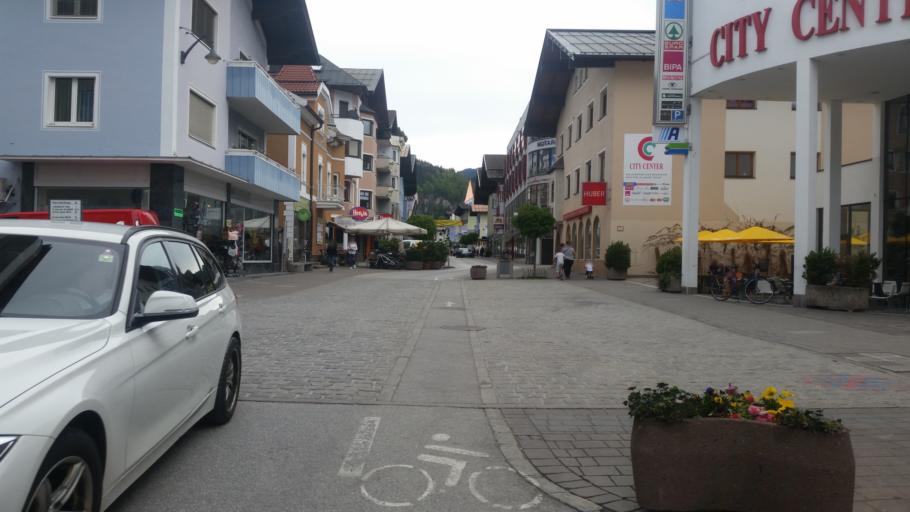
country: AT
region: Tyrol
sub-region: Politischer Bezirk Kufstein
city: Worgl
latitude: 47.4897
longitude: 12.0624
